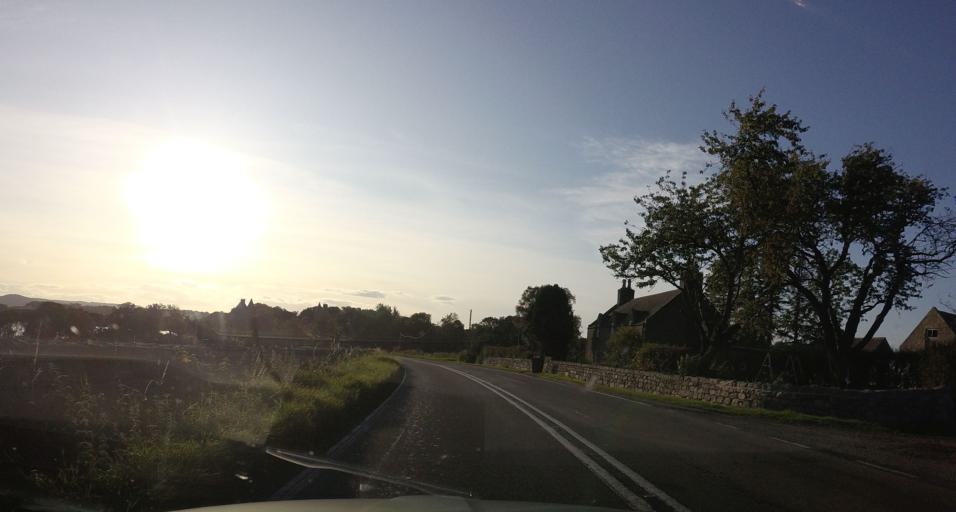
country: GB
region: Scotland
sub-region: Aberdeenshire
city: Westhill
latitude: 57.1631
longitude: -2.3521
